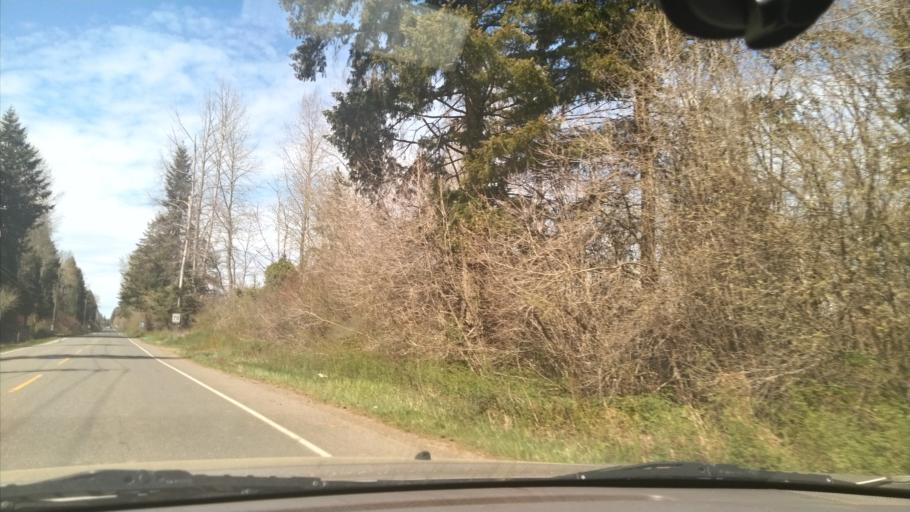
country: CA
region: British Columbia
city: Courtenay
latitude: 49.7010
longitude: -125.0184
